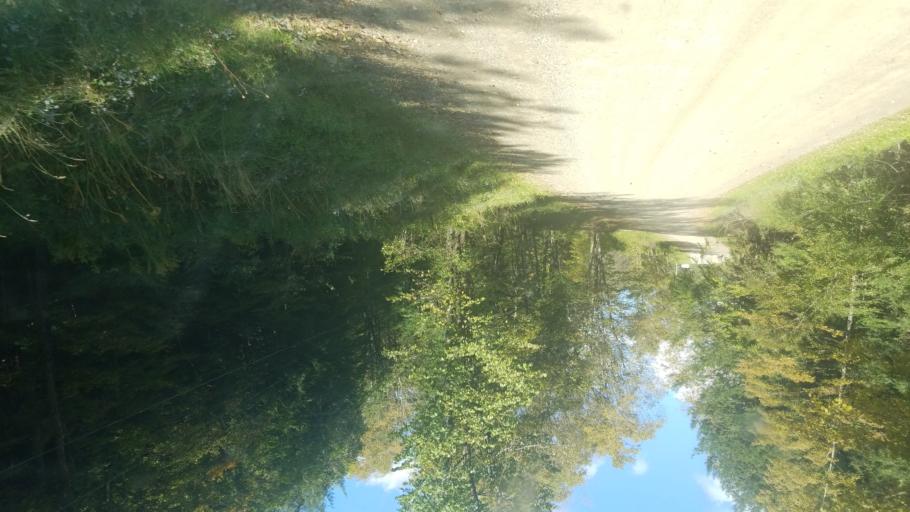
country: US
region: New York
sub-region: Allegany County
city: Cuba
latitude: 42.1722
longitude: -78.3318
